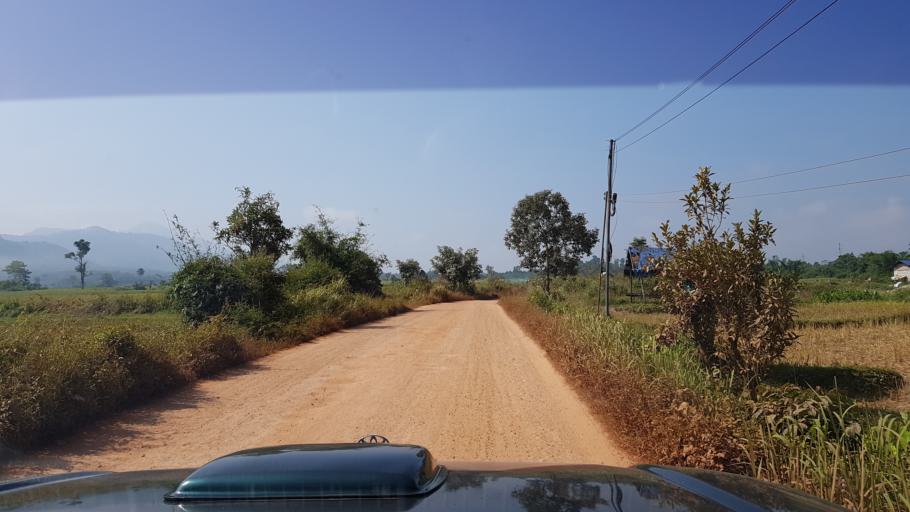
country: LA
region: Oudomxai
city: Muang Xay
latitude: 20.7185
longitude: 102.0442
